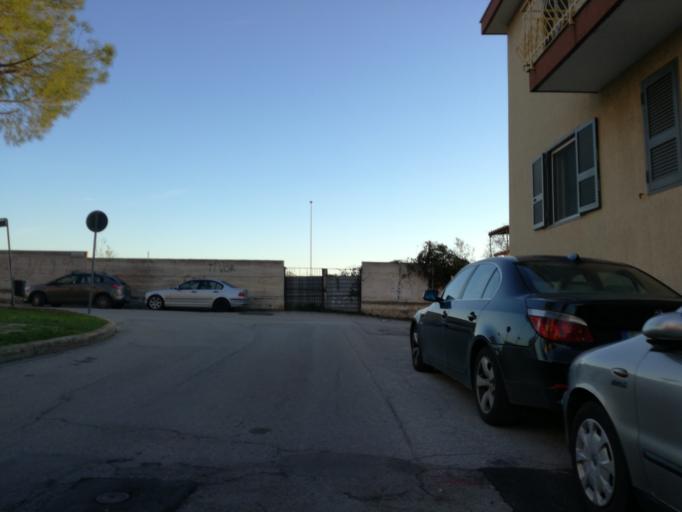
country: IT
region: Apulia
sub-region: Provincia di Bari
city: Adelfia
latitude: 40.9990
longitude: 16.8775
